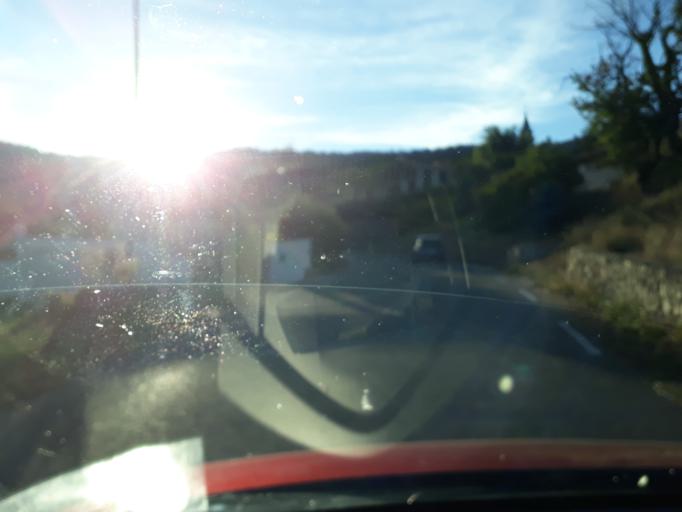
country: FR
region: Rhone-Alpes
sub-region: Departement de l'Ardeche
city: Felines
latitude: 45.3274
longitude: 4.7039
